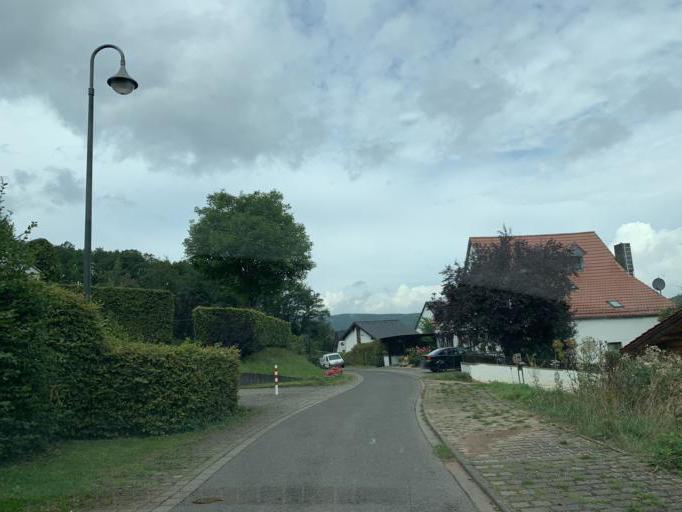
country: DE
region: North Rhine-Westphalia
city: Heimbach
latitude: 50.6500
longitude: 6.4951
